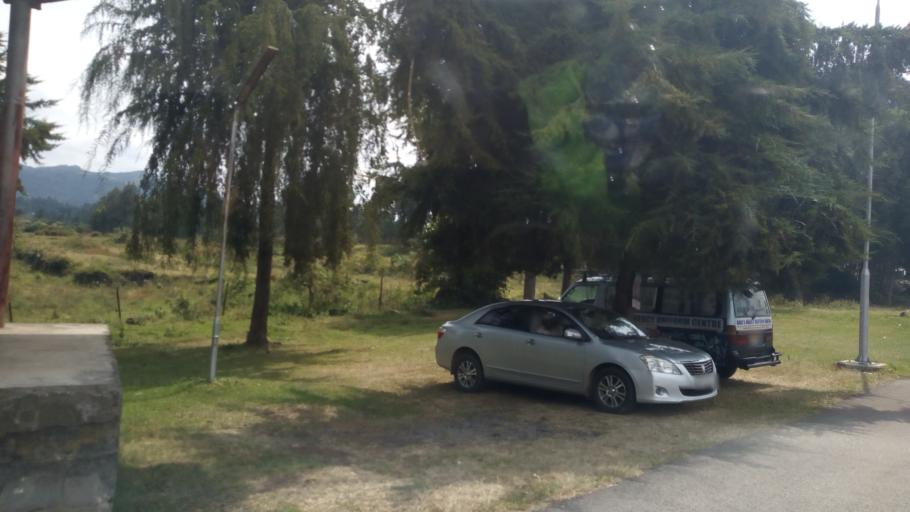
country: UG
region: Western Region
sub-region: Kisoro District
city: Kisoro
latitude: -1.3407
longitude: 29.7399
